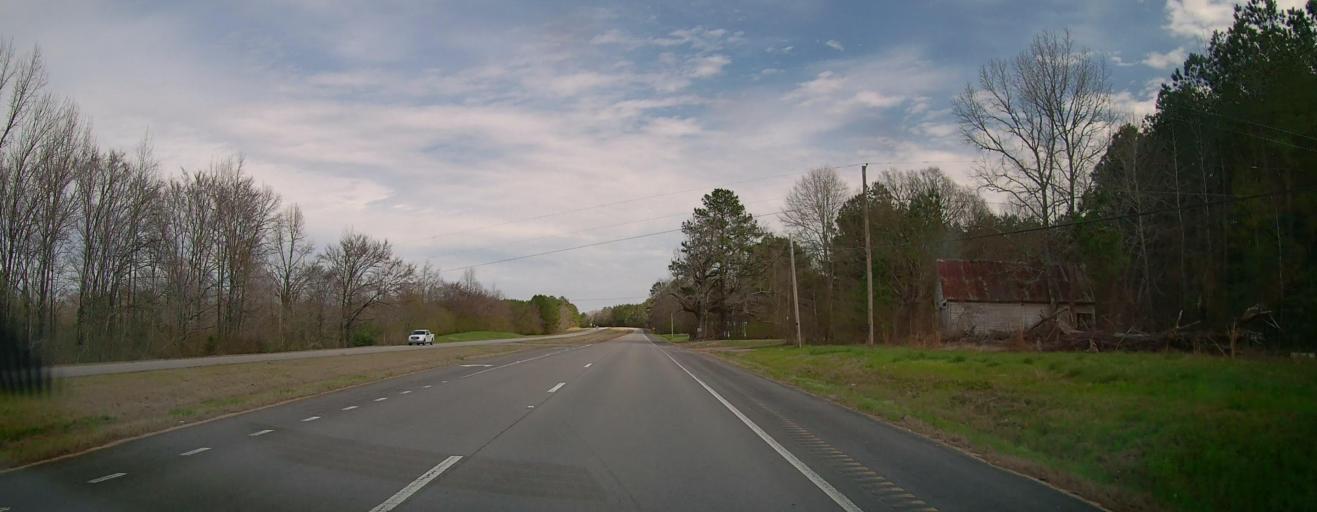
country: US
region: Alabama
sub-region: Marion County
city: Winfield
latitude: 33.9297
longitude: -87.6793
